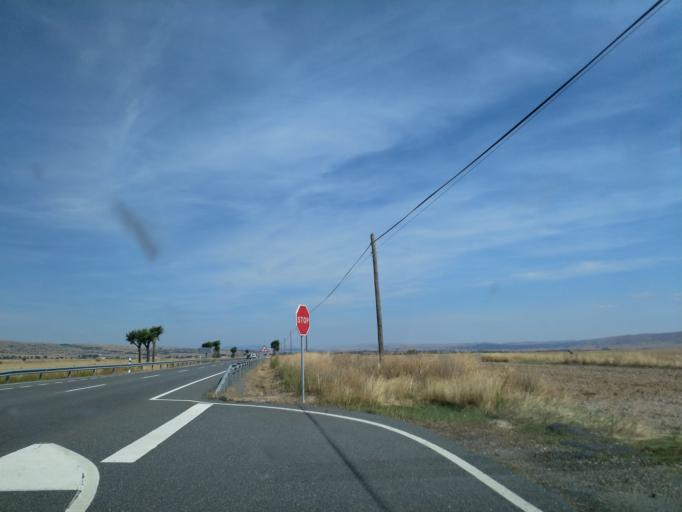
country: ES
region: Castille and Leon
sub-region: Provincia de Avila
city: Munogalindo
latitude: 40.6067
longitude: -4.8754
